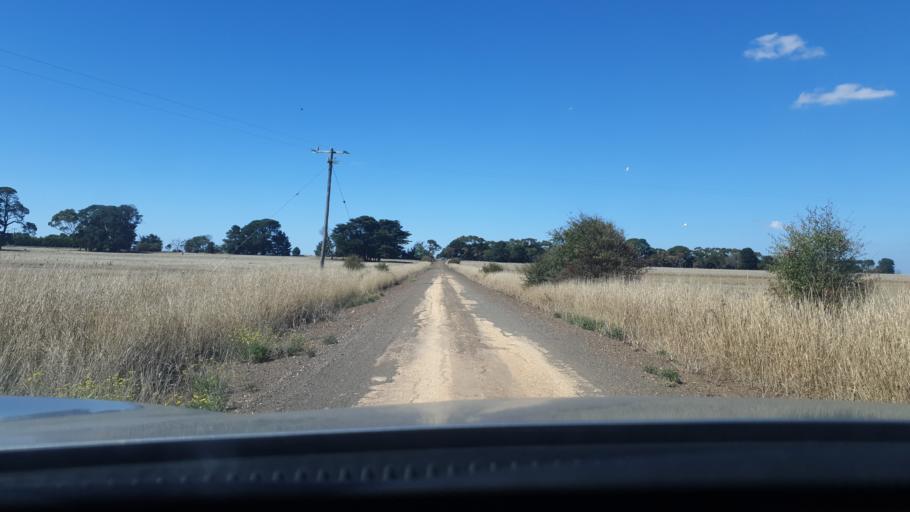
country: AU
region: Victoria
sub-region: Warrnambool
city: Warrnambool
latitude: -38.1648
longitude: 142.3916
